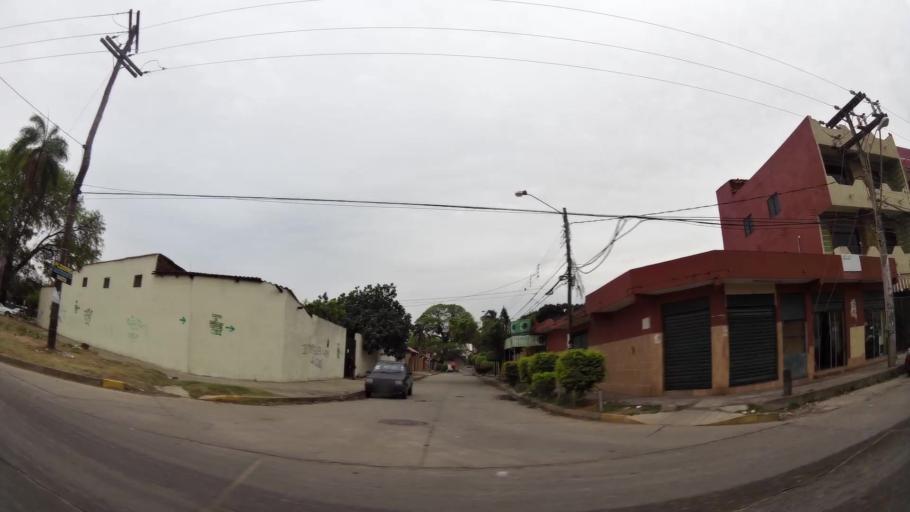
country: BO
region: Santa Cruz
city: Santa Cruz de la Sierra
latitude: -17.8129
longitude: -63.1775
